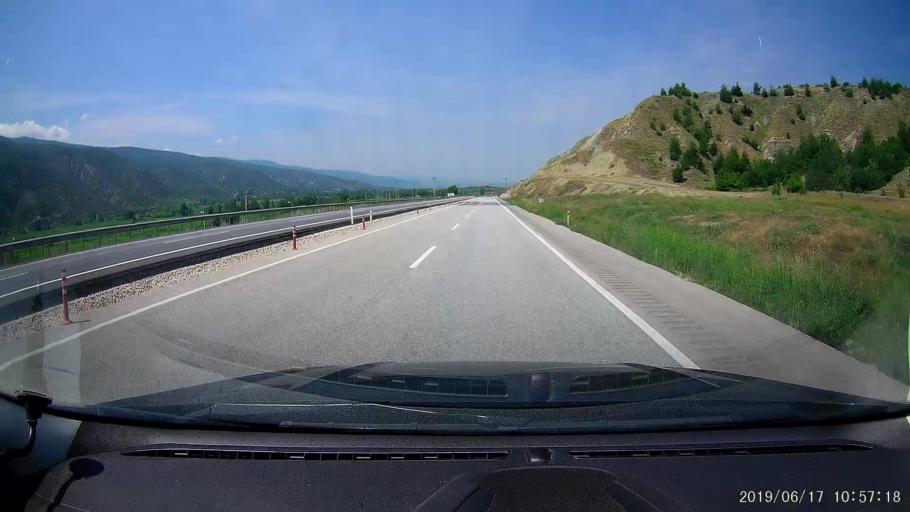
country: TR
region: Corum
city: Hacihamza
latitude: 41.0499
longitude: 34.2490
